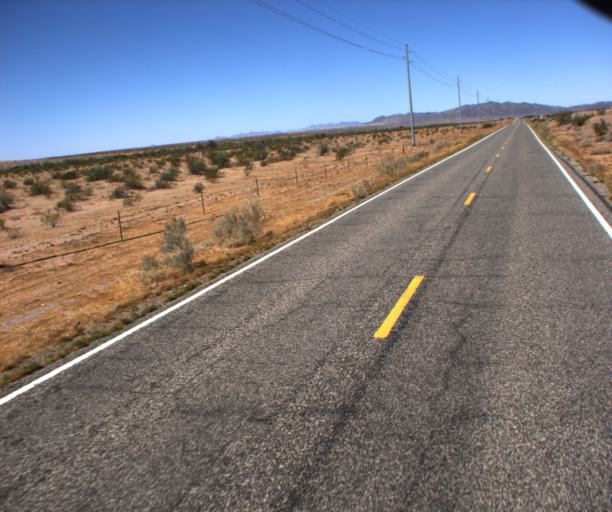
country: US
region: Arizona
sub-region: La Paz County
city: Cienega Springs
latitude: 33.9948
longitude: -114.1510
